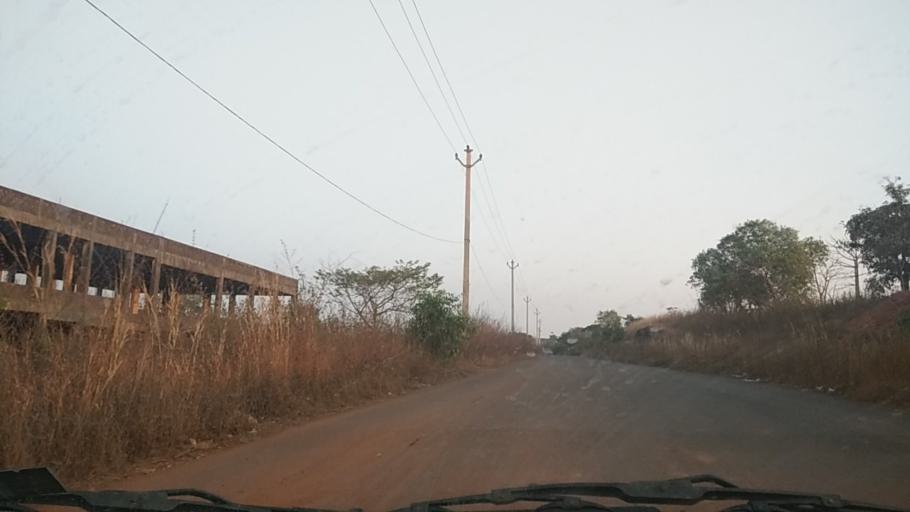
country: IN
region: Goa
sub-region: North Goa
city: Queula
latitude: 15.3607
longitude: 73.9564
